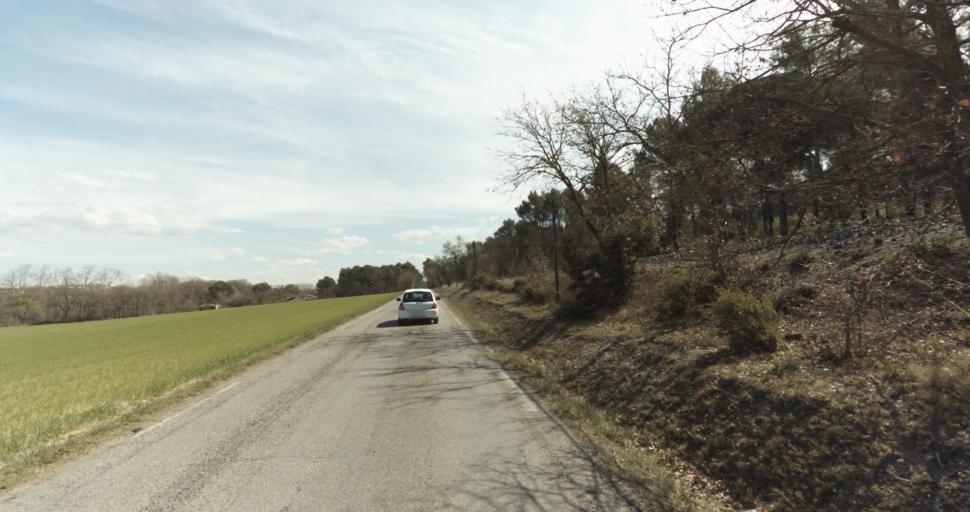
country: FR
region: Provence-Alpes-Cote d'Azur
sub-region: Departement des Bouches-du-Rhone
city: Ventabren
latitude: 43.5096
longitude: 5.3285
